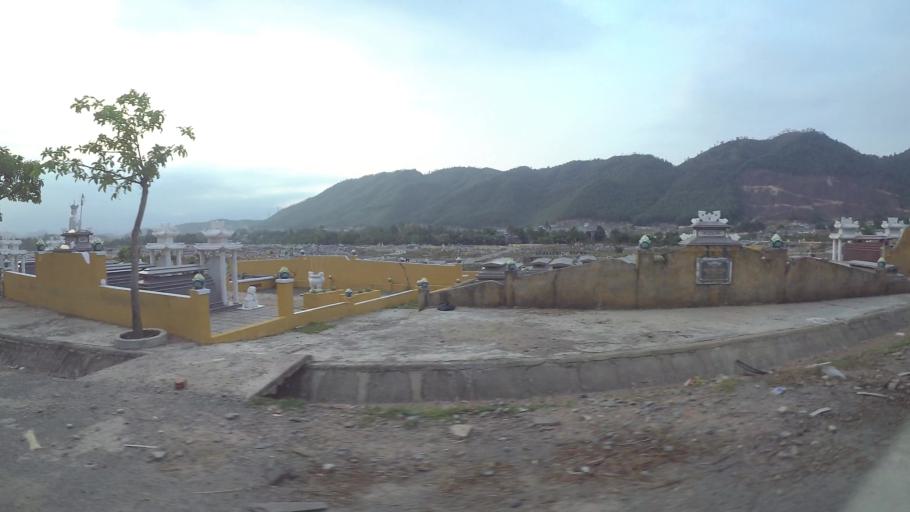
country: VN
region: Da Nang
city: Lien Chieu
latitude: 16.0551
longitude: 108.1254
